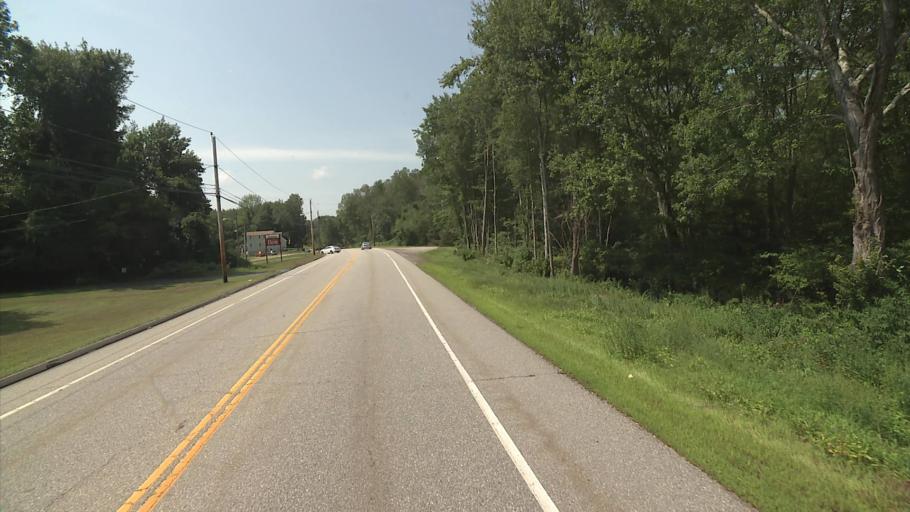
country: US
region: Connecticut
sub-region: New London County
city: Montville Center
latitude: 41.5063
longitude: -72.1359
